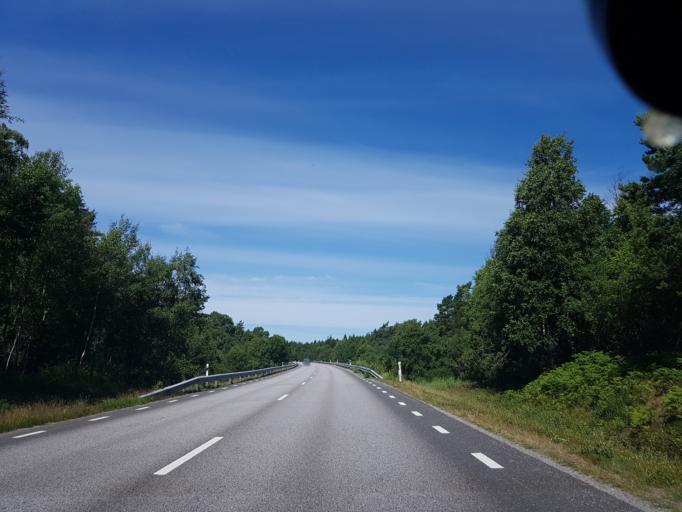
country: SE
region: Vaestra Goetaland
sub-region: Lysekils Kommun
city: Lysekil
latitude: 58.1562
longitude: 11.5199
